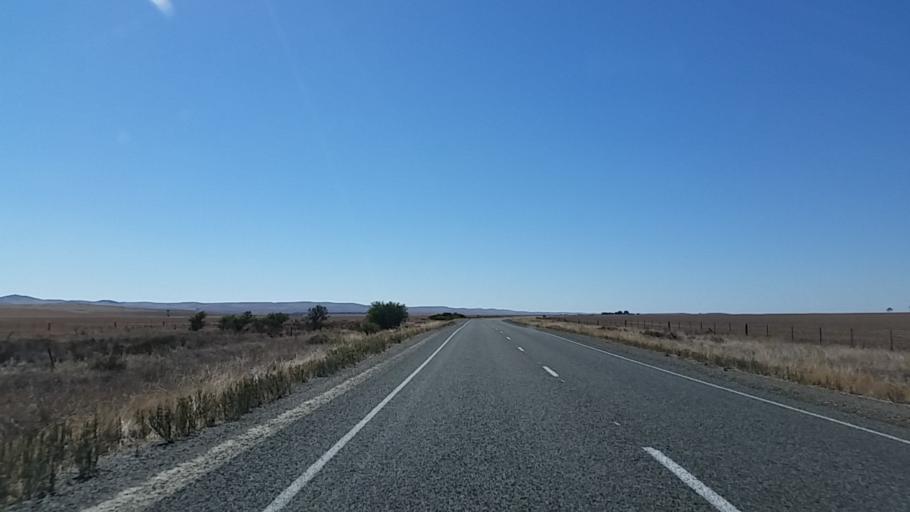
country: AU
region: South Australia
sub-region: Northern Areas
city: Jamestown
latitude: -33.2723
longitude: 138.8683
